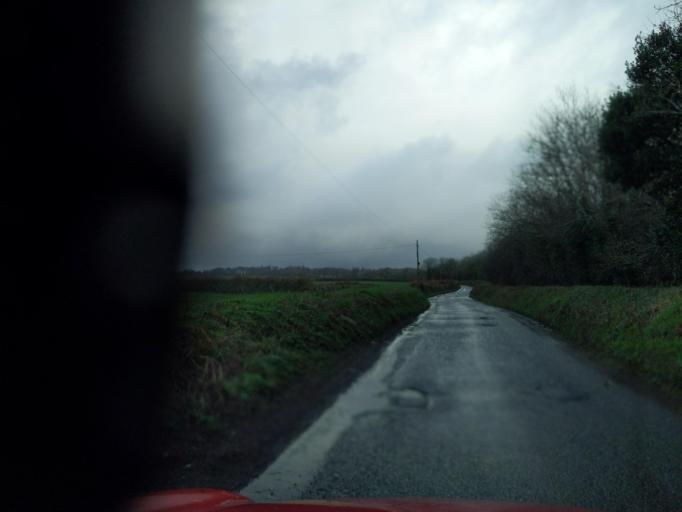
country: GB
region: England
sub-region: Devon
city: Yelverton
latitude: 50.4442
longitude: -4.1244
